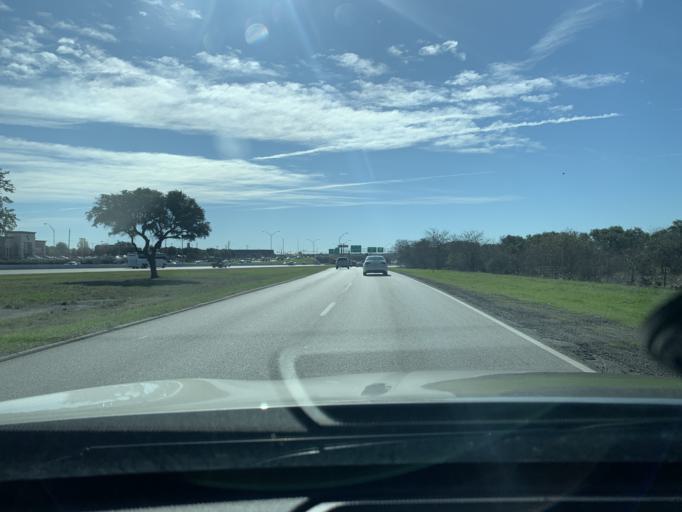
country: US
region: Texas
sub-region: Williamson County
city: Round Rock
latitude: 30.5627
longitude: -97.6934
